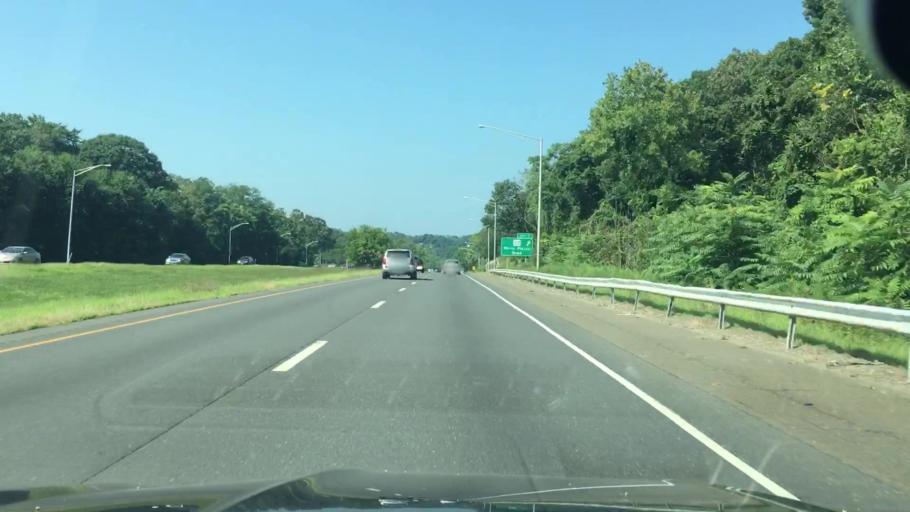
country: US
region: Connecticut
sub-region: Fairfield County
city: Trumbull
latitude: 41.2254
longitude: -73.1687
